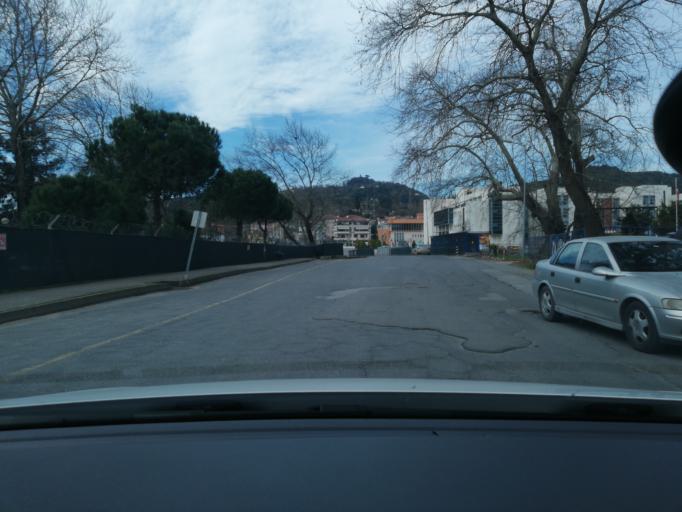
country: TR
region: Zonguldak
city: Eregli
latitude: 41.2900
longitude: 31.4086
